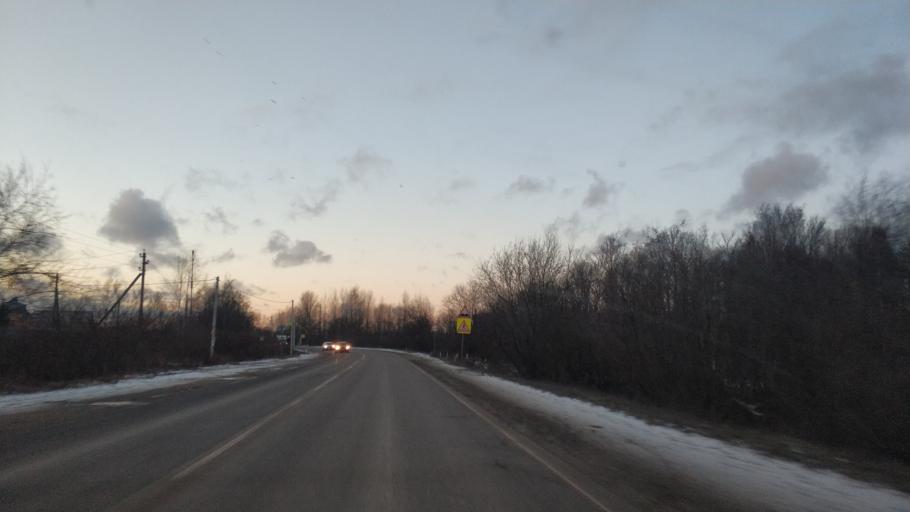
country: RU
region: St.-Petersburg
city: Pontonnyy
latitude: 59.8060
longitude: 30.6233
